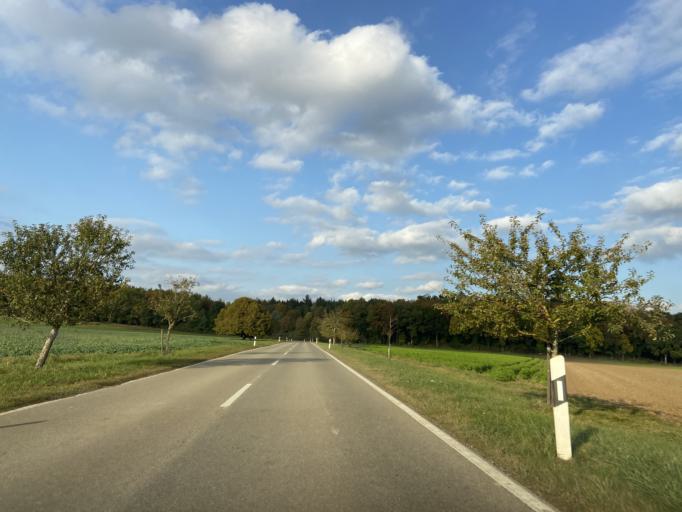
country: DE
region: Baden-Wuerttemberg
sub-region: Tuebingen Region
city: Scheer
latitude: 48.1004
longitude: 9.3353
